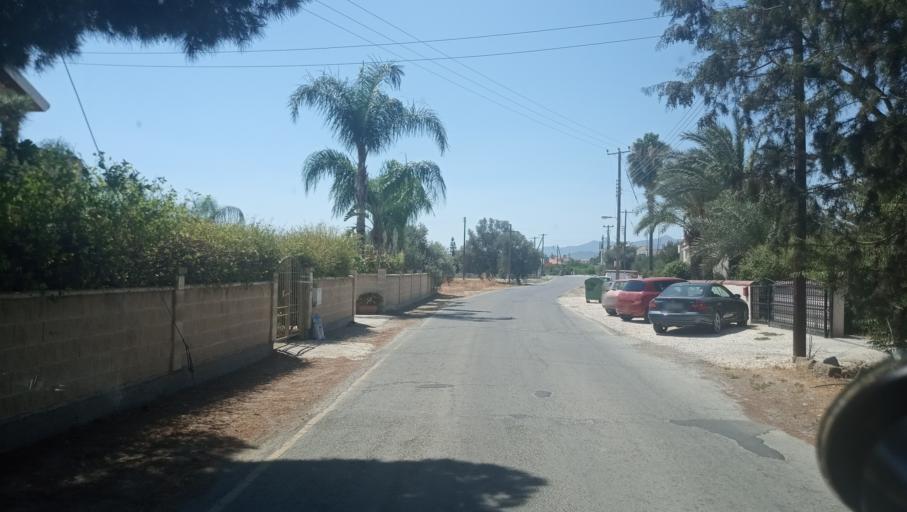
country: CY
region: Lefkosia
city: Psimolofou
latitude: 35.0678
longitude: 33.2599
